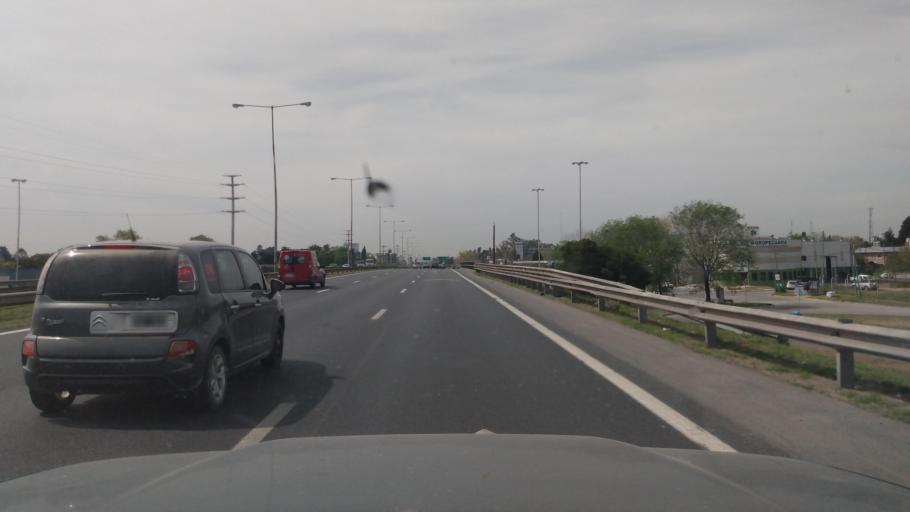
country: AR
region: Buenos Aires
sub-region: Partido de Pilar
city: Pilar
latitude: -34.4521
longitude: -58.9242
